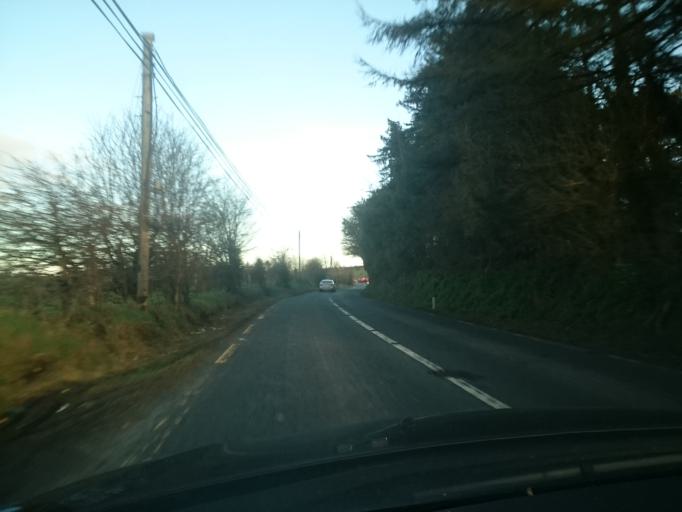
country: IE
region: Connaught
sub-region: Maigh Eo
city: Kiltamagh
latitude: 53.7995
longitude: -9.1055
